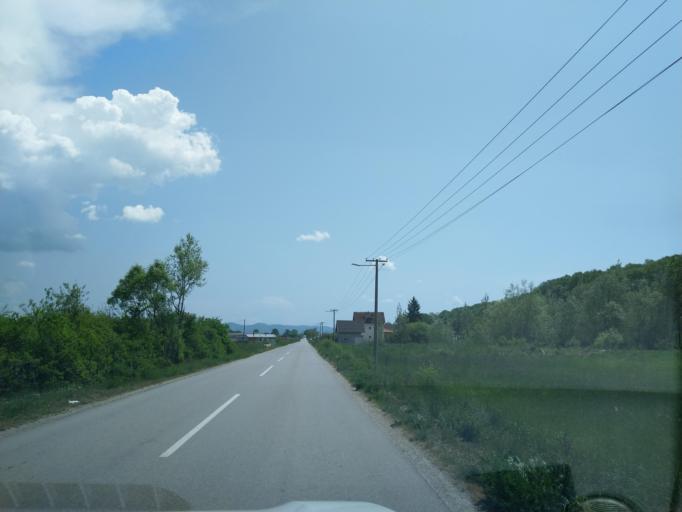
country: RS
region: Central Serbia
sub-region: Zlatiborski Okrug
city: Pozega
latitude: 43.8557
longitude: 19.9832
